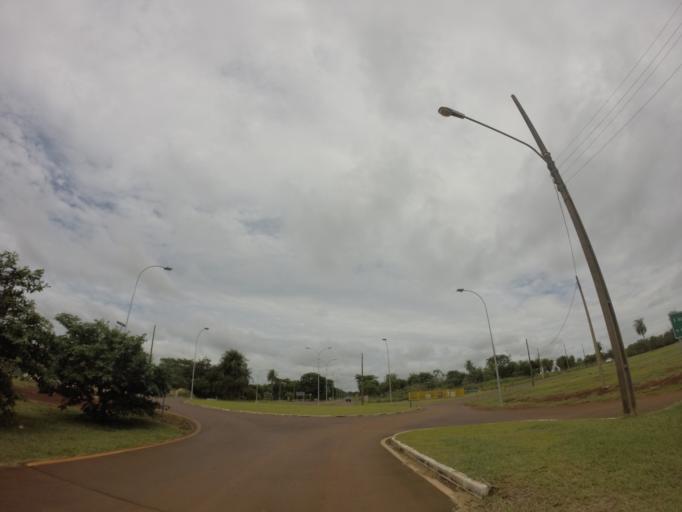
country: PY
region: Alto Parana
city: Ciudad del Este
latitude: -25.3904
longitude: -54.6261
